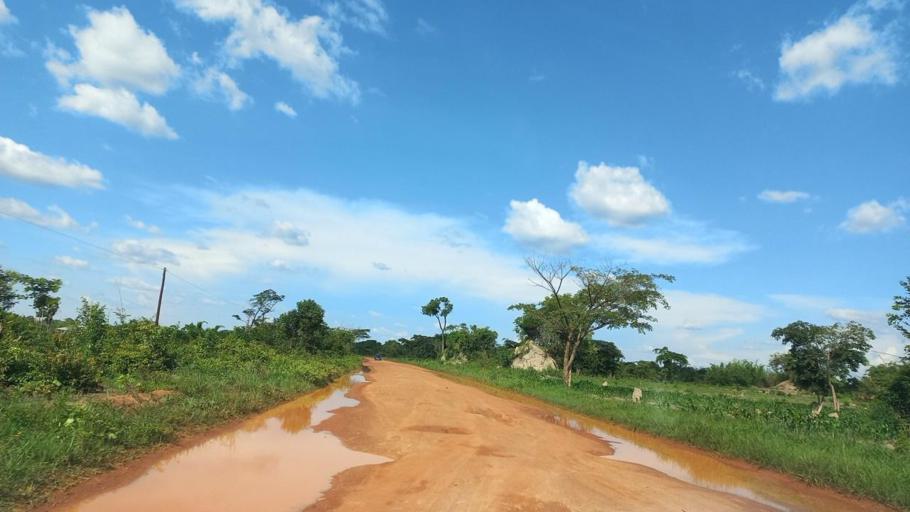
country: ZM
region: Copperbelt
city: Kitwe
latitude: -12.8554
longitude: 28.3872
